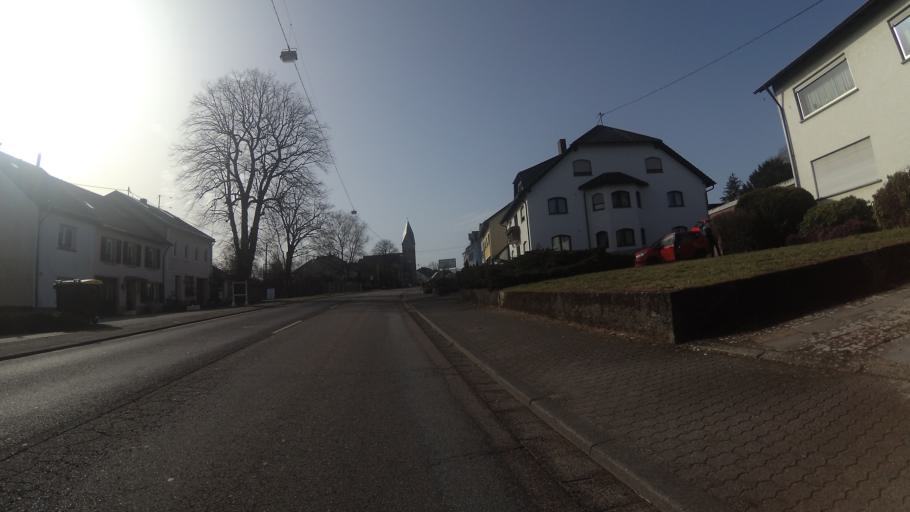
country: DE
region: Saarland
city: Saarlouis
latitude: 49.2877
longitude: 6.7319
